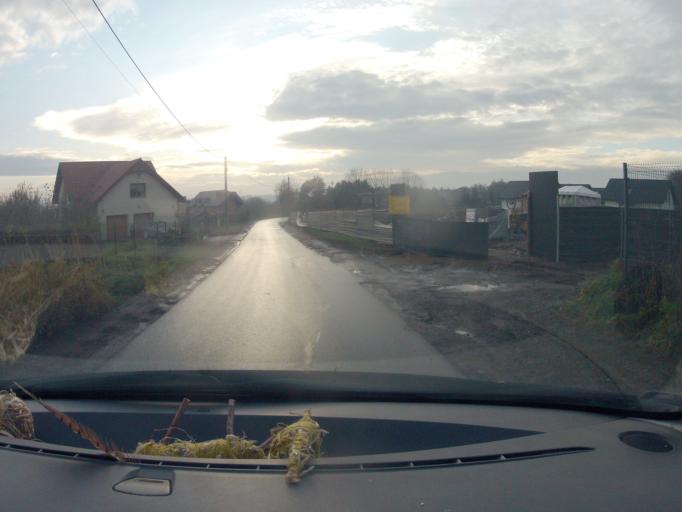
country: PL
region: Lesser Poland Voivodeship
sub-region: Krakow
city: Sidzina
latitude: 49.9986
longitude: 19.8836
